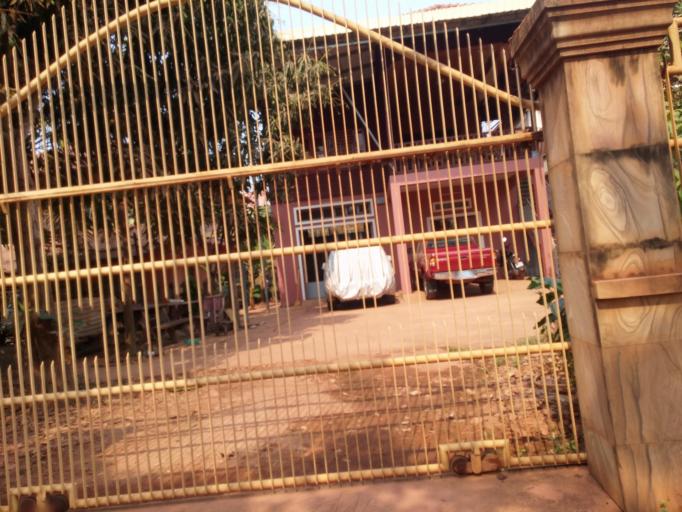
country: KH
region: Siem Reap
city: Siem Reap
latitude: 13.3731
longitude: 103.8481
